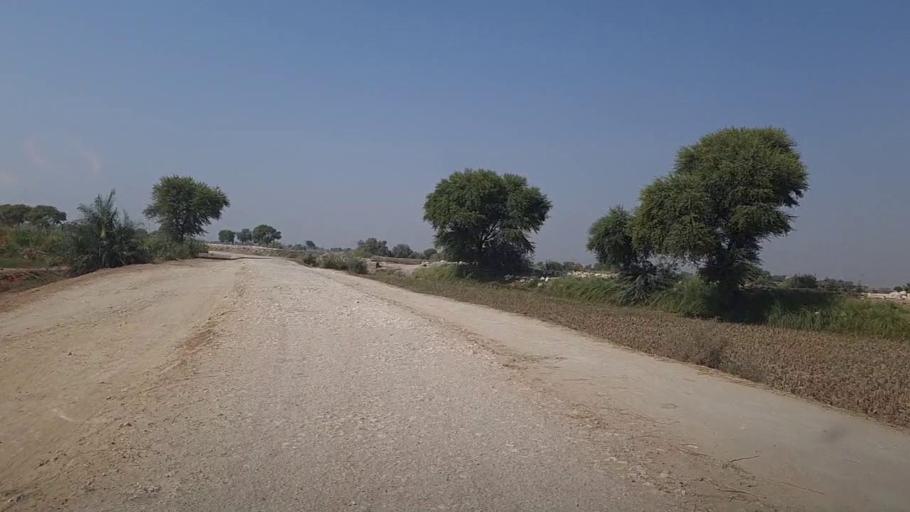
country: PK
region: Sindh
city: Kandhkot
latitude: 28.3899
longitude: 69.3363
